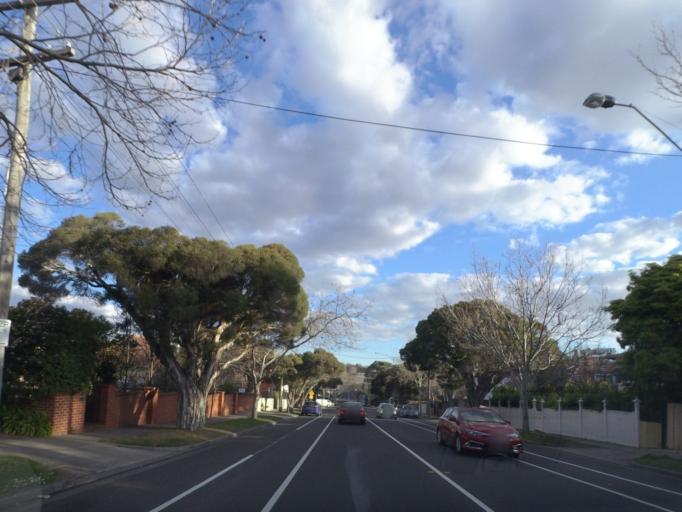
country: AU
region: Victoria
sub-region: Whitehorse
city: Surrey Hills
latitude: -37.8217
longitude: 145.0981
